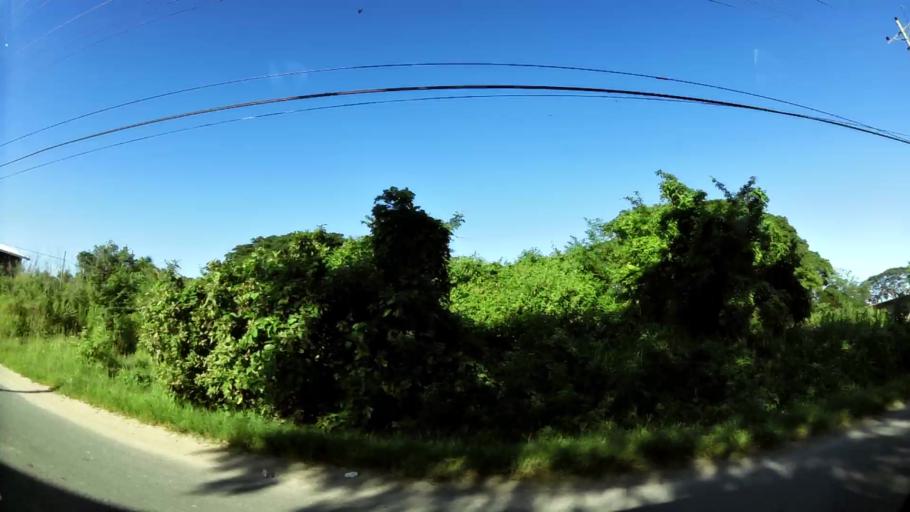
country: TT
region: Tobago
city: Scarborough
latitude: 11.1548
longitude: -60.8135
